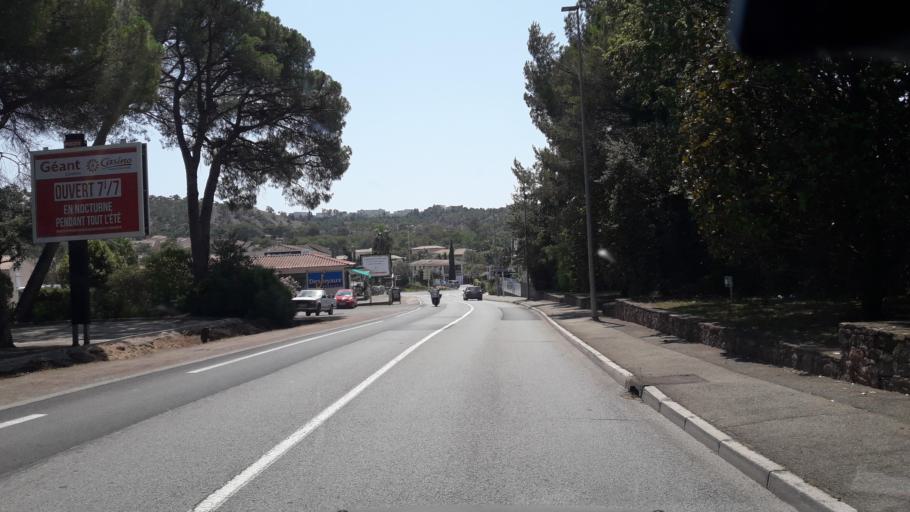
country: FR
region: Provence-Alpes-Cote d'Azur
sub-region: Departement du Var
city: Saint-Raphael
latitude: 43.4395
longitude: 6.7833
